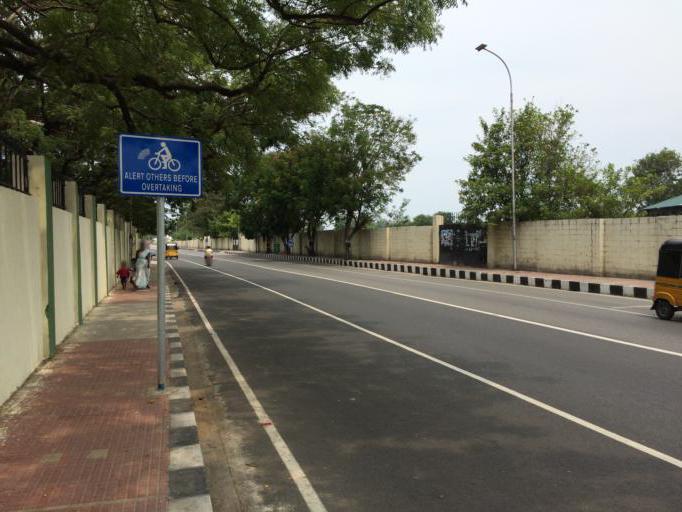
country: IN
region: Tamil Nadu
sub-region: Chennai
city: Chennai
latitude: 13.0763
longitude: 80.2836
